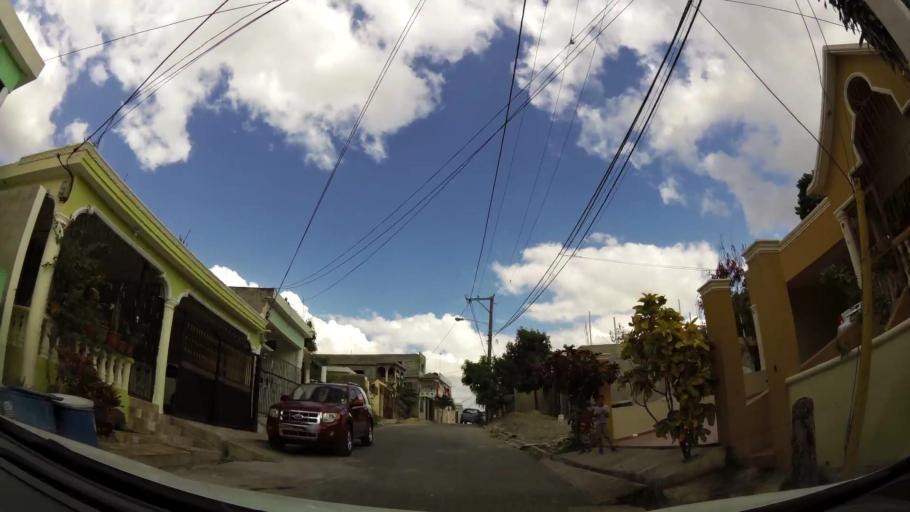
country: DO
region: Nacional
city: Ensanche Luperon
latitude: 18.5310
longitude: -69.8975
